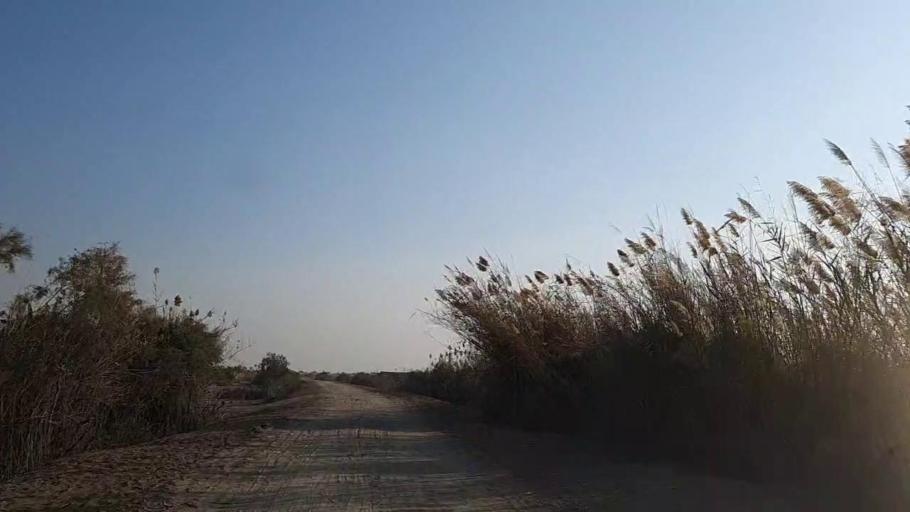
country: PK
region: Sindh
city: Daur
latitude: 26.4304
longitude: 68.3530
